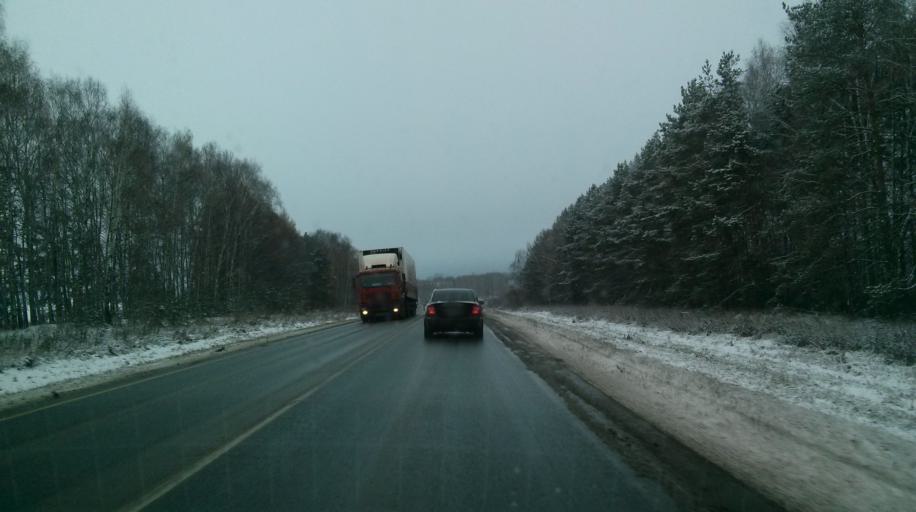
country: RU
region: Nizjnij Novgorod
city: Vorsma
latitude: 56.0450
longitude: 43.3892
